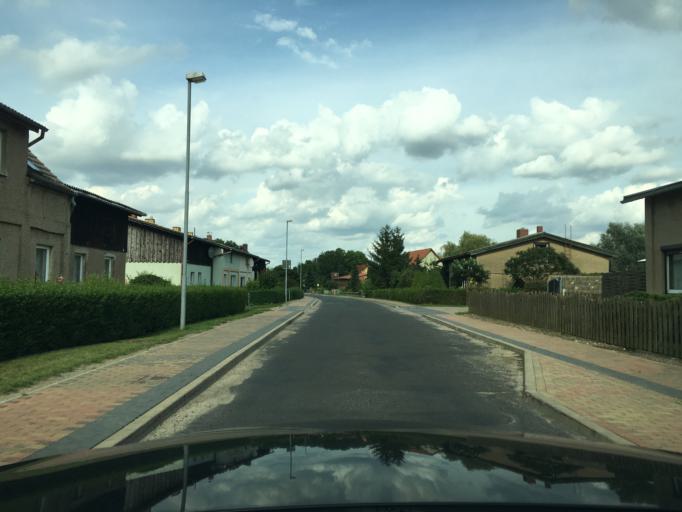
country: DE
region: Mecklenburg-Vorpommern
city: Mollenhagen
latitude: 53.5015
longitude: 12.9250
